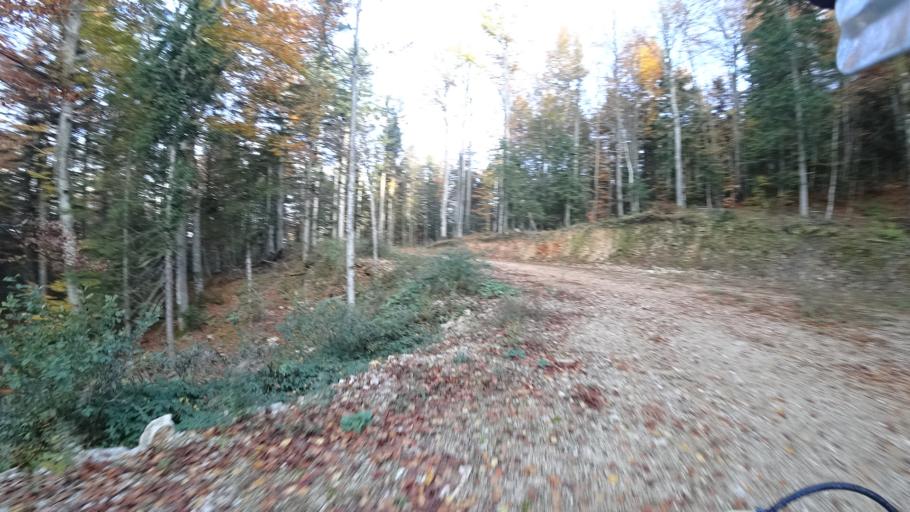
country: HR
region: Karlovacka
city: Plaski
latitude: 44.9658
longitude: 15.3903
